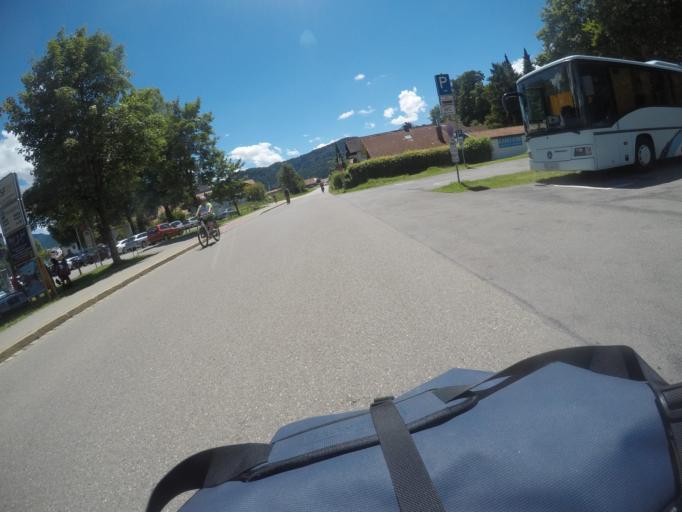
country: DE
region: Bavaria
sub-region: Swabia
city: Fuessen
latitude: 47.5809
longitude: 10.7091
